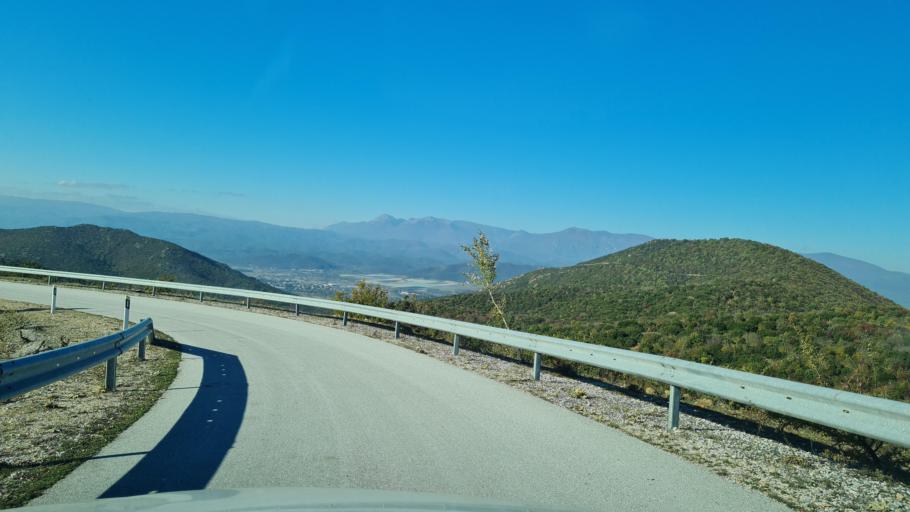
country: MK
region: Bogdanci
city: Bogdanci
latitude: 41.2275
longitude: 22.5527
